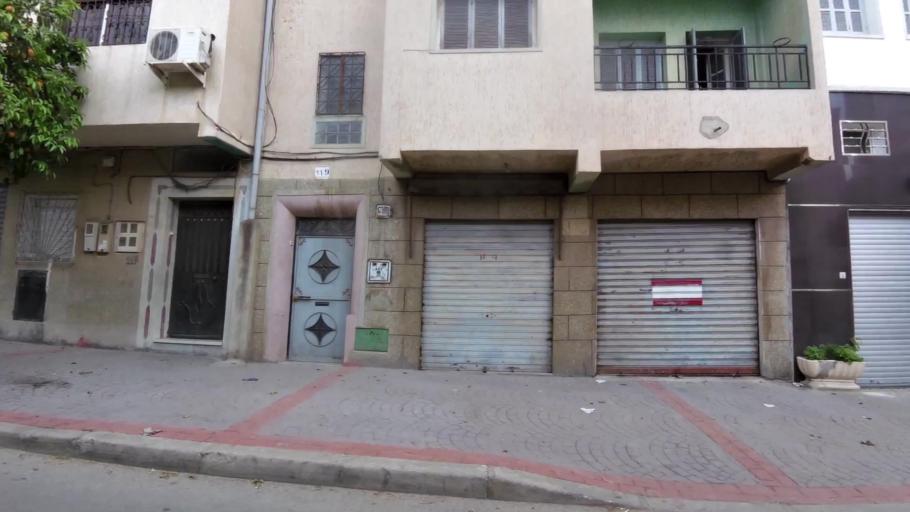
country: MA
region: Tanger-Tetouan
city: Tetouan
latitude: 35.5687
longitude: -5.3566
